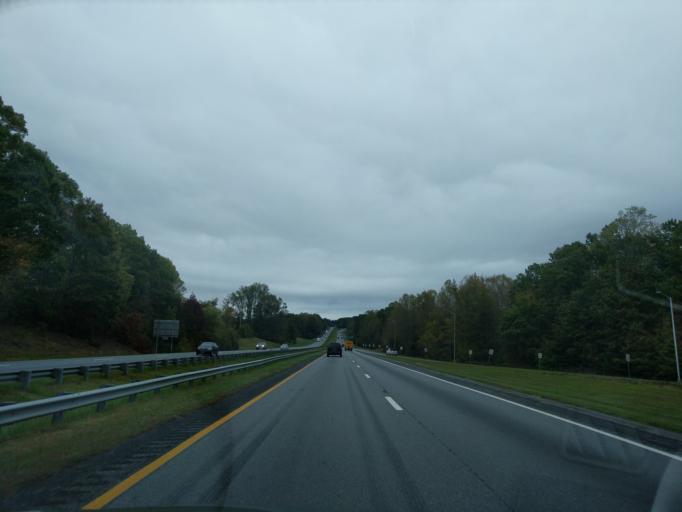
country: US
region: North Carolina
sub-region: Cleveland County
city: White Plains
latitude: 35.1849
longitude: -81.4068
